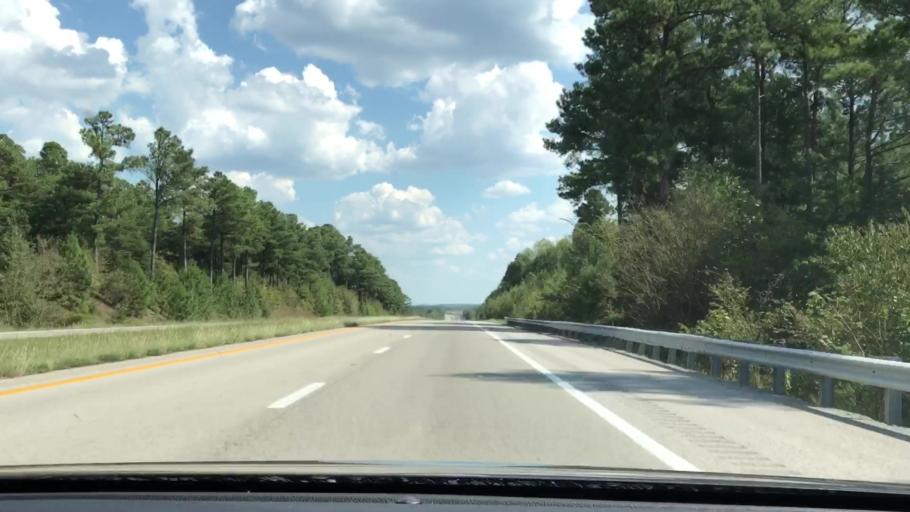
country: US
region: Kentucky
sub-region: Hopkins County
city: Dawson Springs
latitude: 37.1943
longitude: -87.6344
